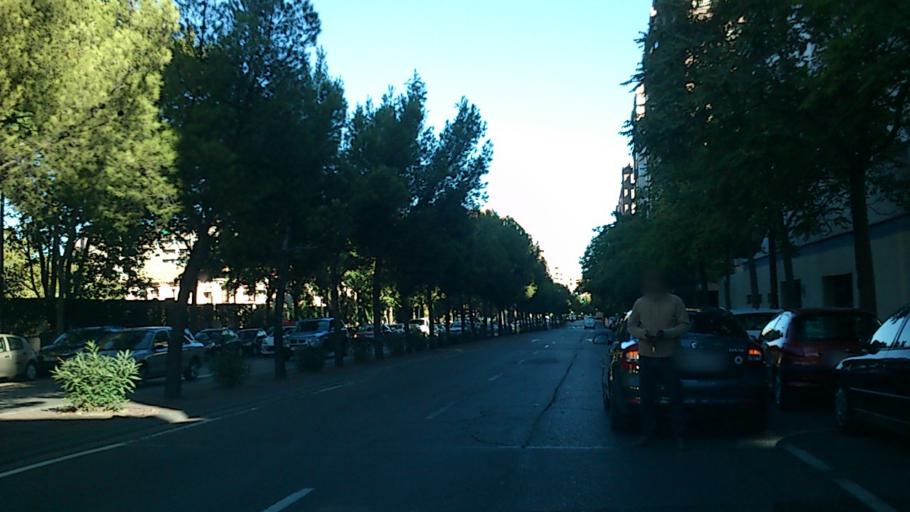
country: ES
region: Aragon
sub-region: Provincia de Zaragoza
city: Delicias
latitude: 41.6475
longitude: -0.9080
